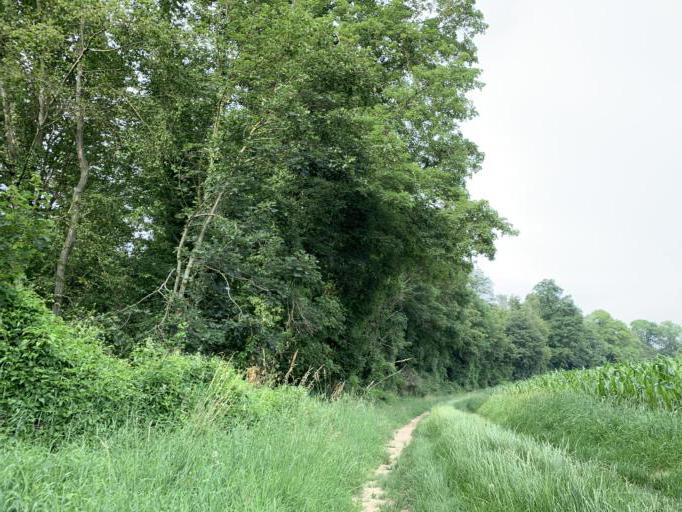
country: FR
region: Alsace
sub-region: Departement du Haut-Rhin
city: Morschwiller-le-Bas
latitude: 47.7251
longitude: 7.2663
